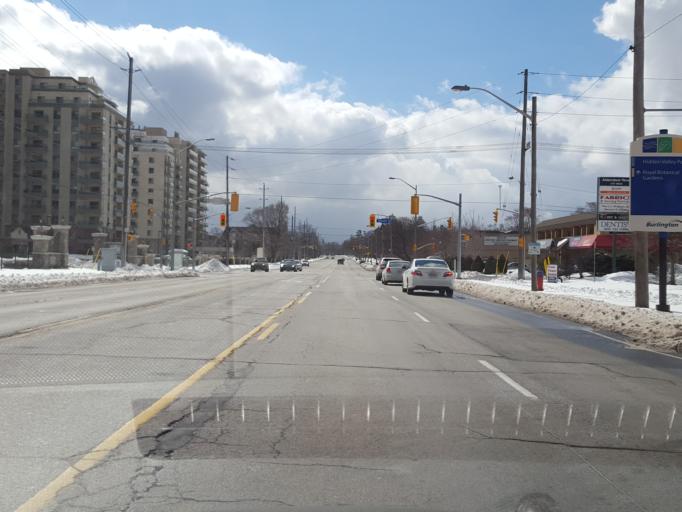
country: CA
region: Ontario
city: Hamilton
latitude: 43.3043
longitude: -79.8560
